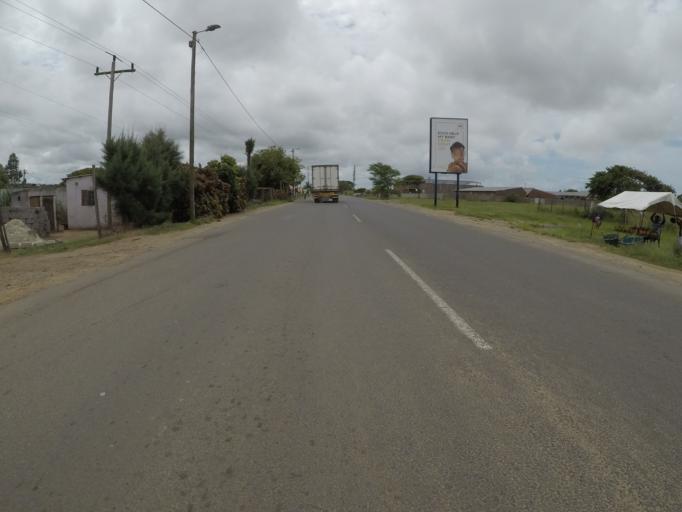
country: ZA
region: KwaZulu-Natal
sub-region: uThungulu District Municipality
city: eSikhawini
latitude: -28.8665
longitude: 31.9074
